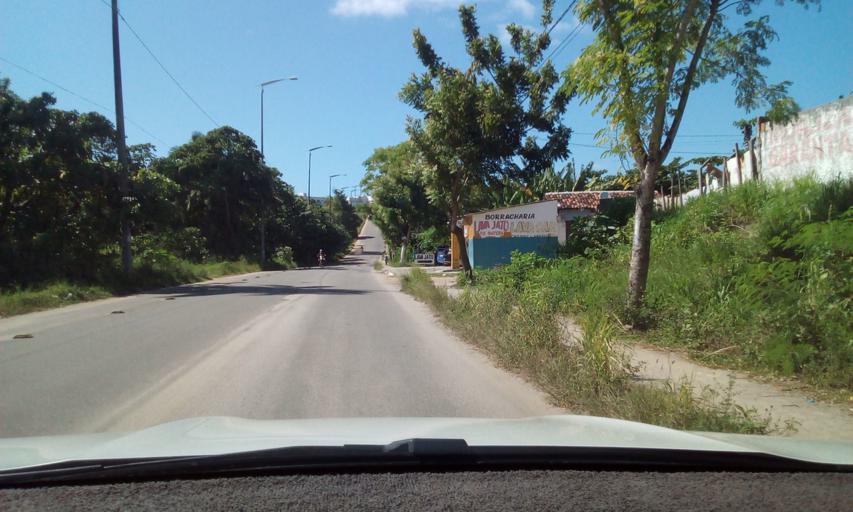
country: BR
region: Paraiba
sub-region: Joao Pessoa
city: Joao Pessoa
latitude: -7.1949
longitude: -34.8382
